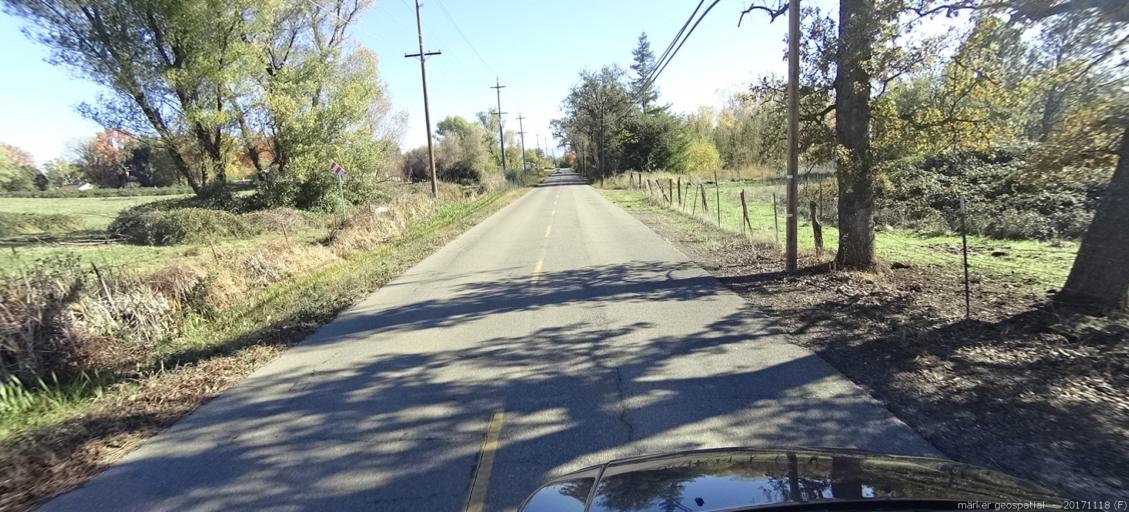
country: US
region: California
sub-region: Shasta County
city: Cottonwood
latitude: 40.3965
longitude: -122.2586
